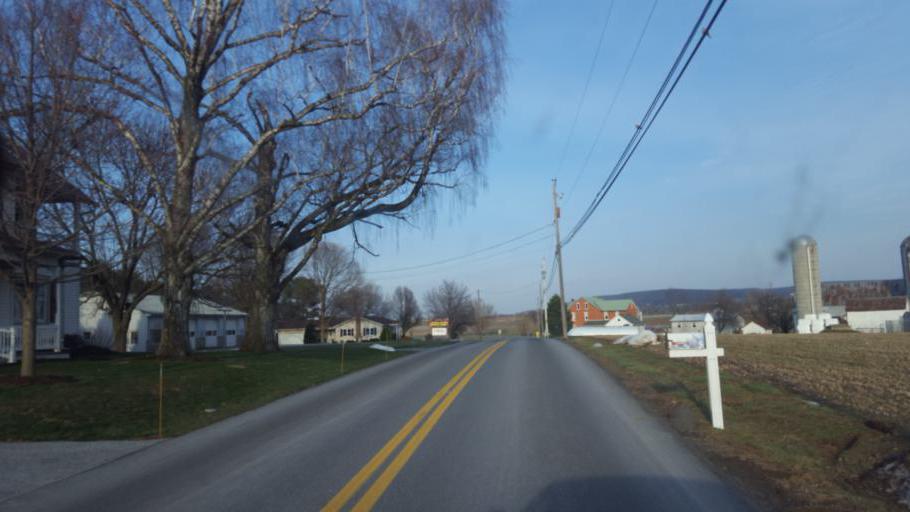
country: US
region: Pennsylvania
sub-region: Lancaster County
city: New Holland
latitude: 40.0877
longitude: -76.0870
